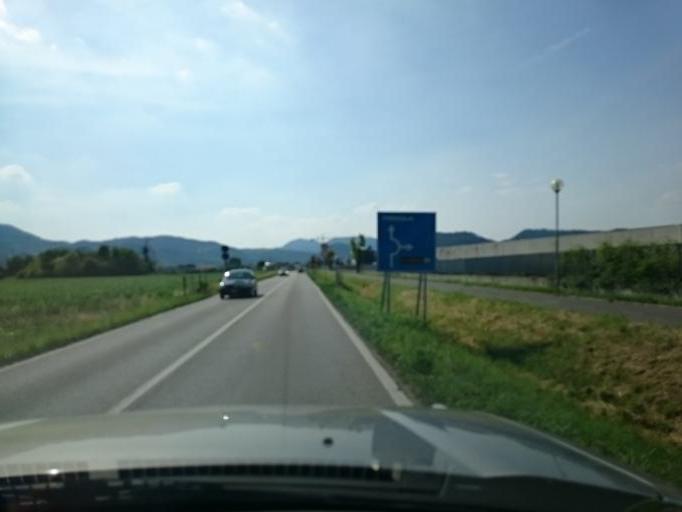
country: IT
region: Veneto
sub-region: Provincia di Padova
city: Torreglia
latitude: 45.3327
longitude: 11.7578
